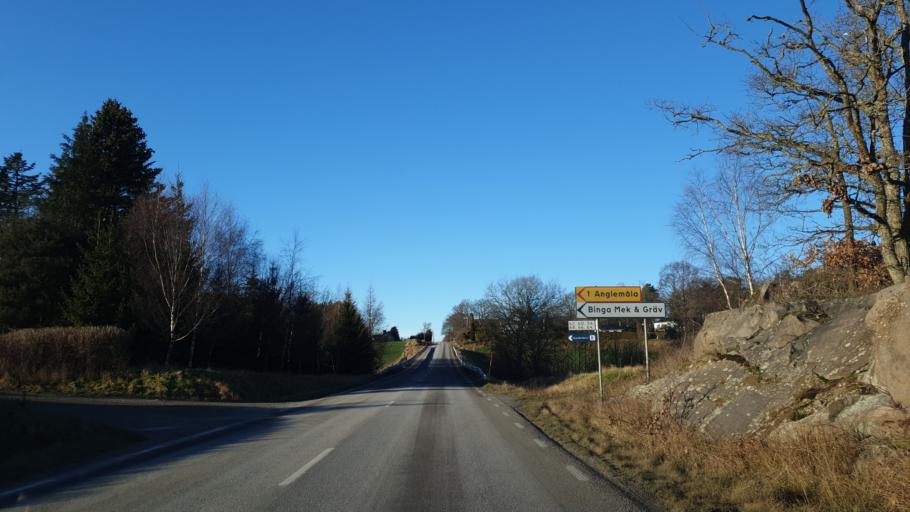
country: SE
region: Blekinge
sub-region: Ronneby Kommun
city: Ronneby
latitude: 56.1959
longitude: 15.3371
